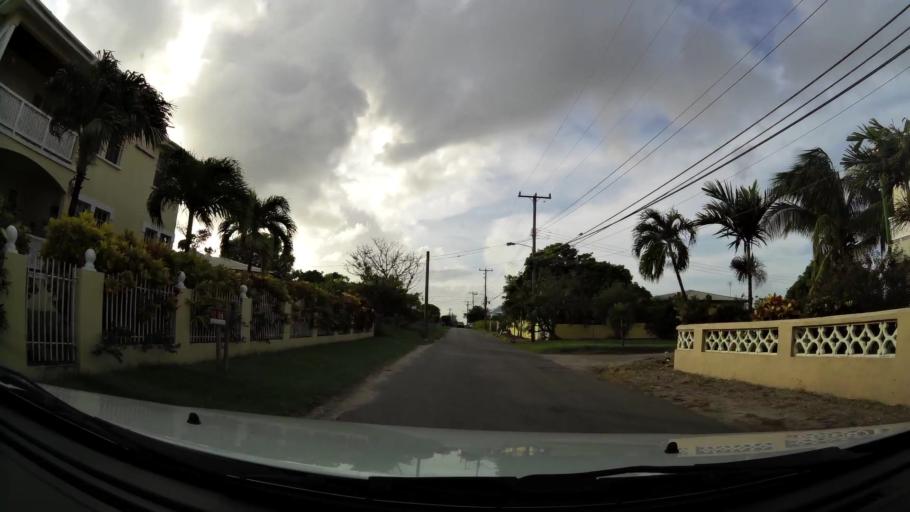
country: BB
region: Christ Church
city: Oistins
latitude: 13.0516
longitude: -59.5302
